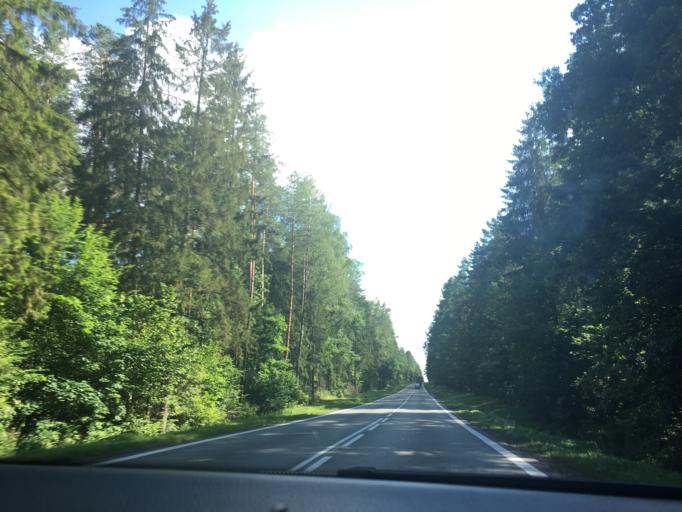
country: PL
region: Podlasie
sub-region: Powiat bialostocki
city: Wasilkow
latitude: 53.3189
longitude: 23.1282
